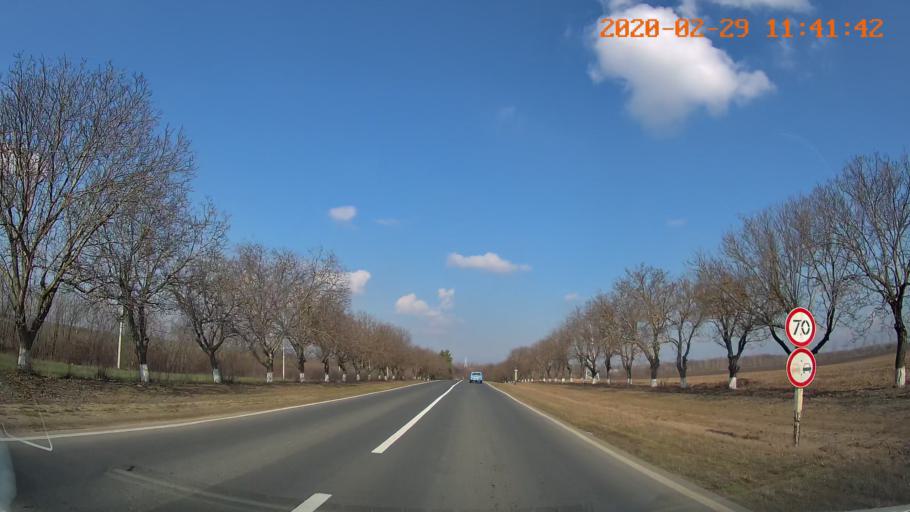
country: MD
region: Rezina
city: Saharna
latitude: 47.6753
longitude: 29.0155
